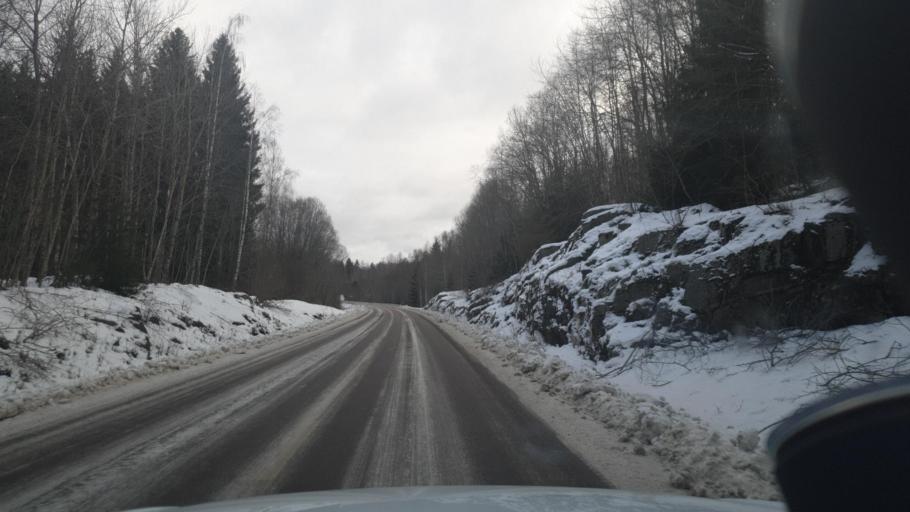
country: SE
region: Vaermland
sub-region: Eda Kommun
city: Amotfors
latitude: 59.7140
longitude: 12.2879
